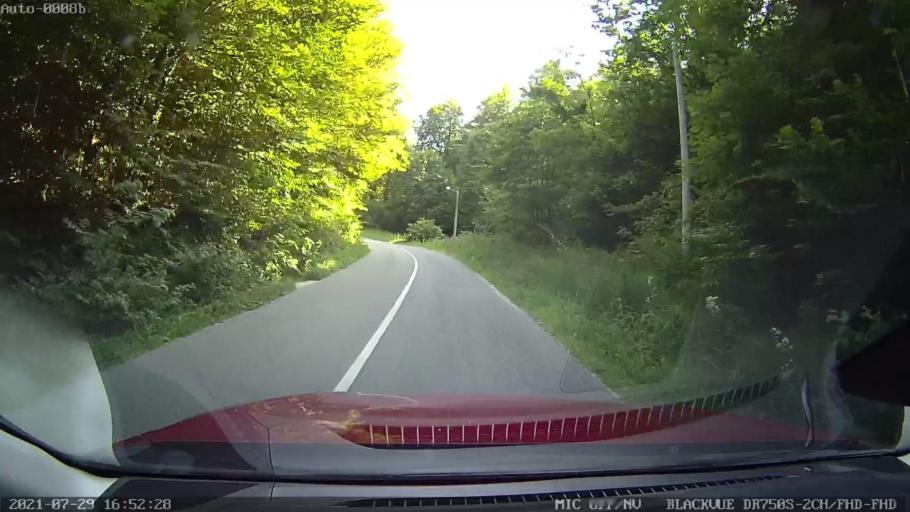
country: HR
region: Varazdinska
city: Ivanec
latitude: 46.2032
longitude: 16.1342
